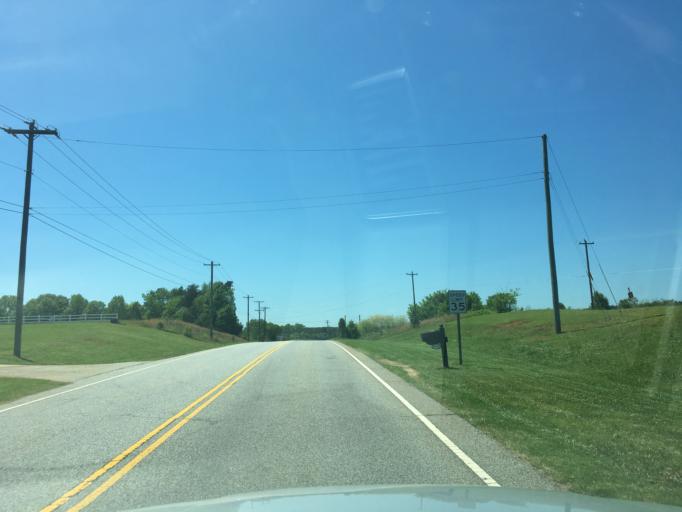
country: US
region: South Carolina
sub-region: Greenville County
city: Greer
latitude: 34.8839
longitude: -82.1925
